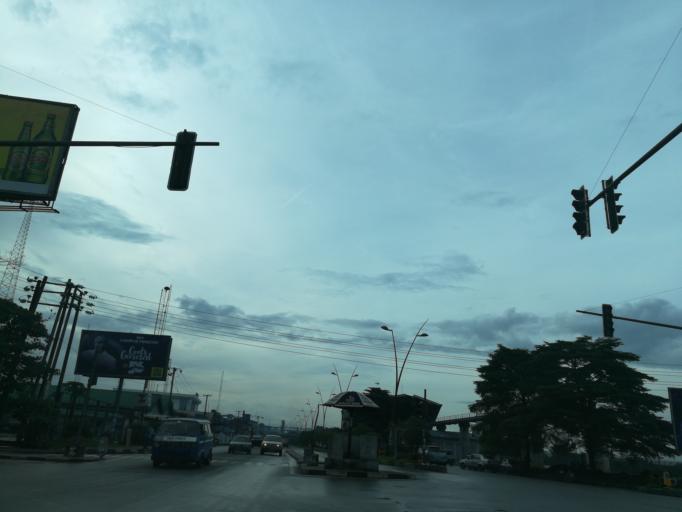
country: NG
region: Rivers
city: Port Harcourt
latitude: 4.7827
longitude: 7.0058
